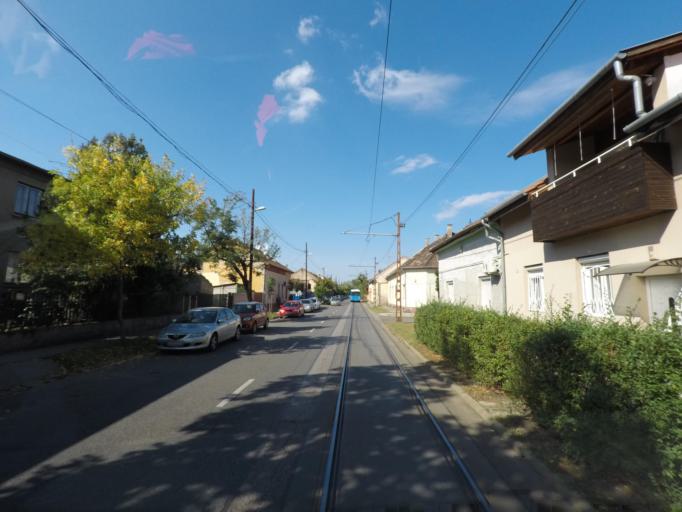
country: HU
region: Budapest
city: Budapest XX. keruelet
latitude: 47.4468
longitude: 19.1074
